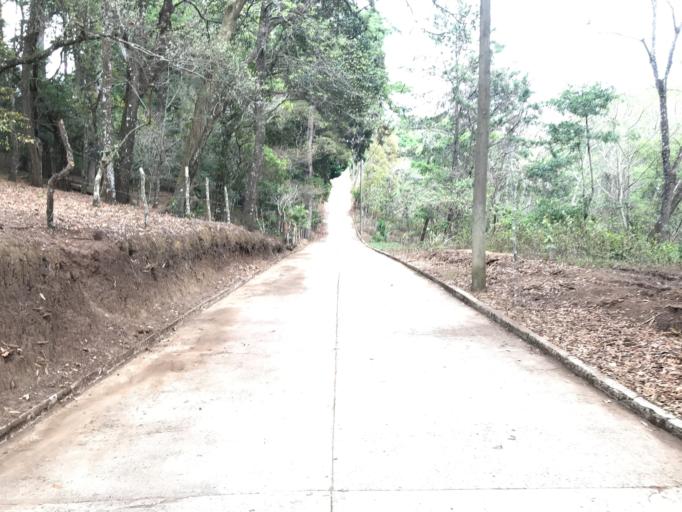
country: GT
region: Guatemala
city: Santa Catarina Pinula
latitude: 14.5393
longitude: -90.4903
